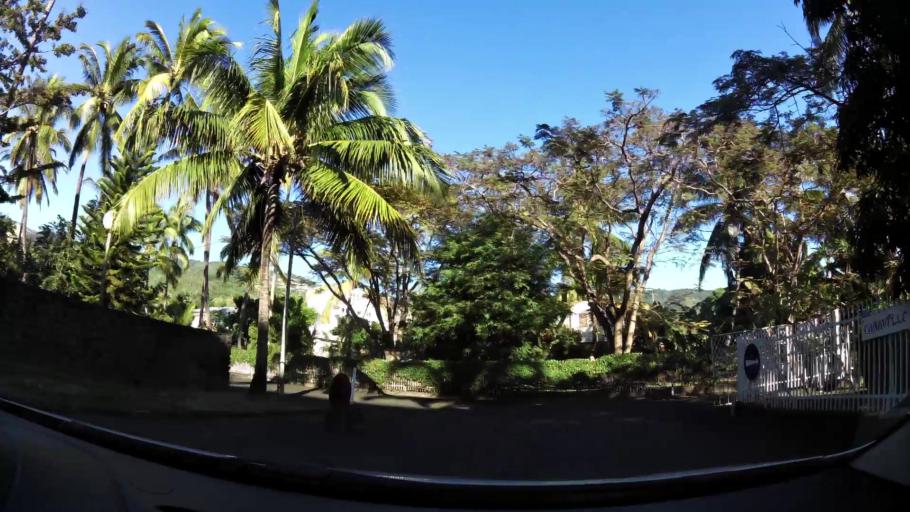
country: RE
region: Reunion
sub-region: Reunion
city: Saint-Denis
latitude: -20.8919
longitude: 55.4574
